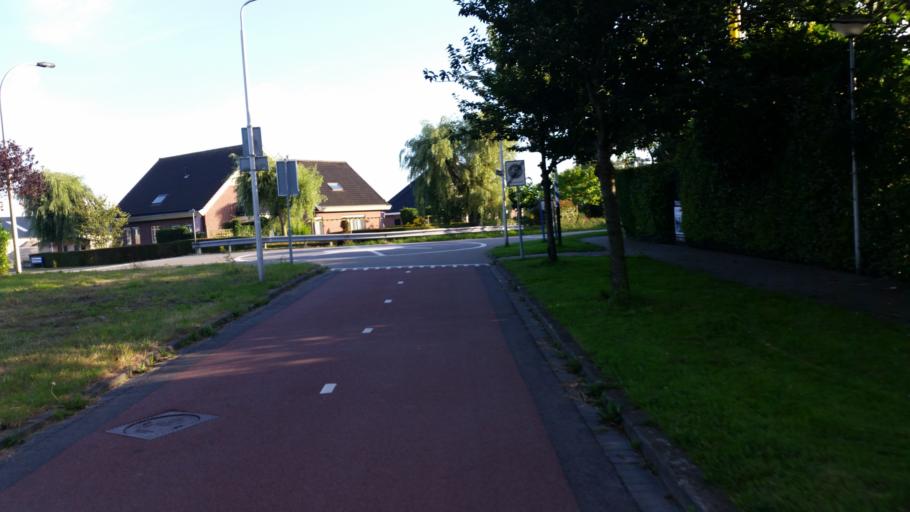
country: NL
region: South Holland
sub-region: Gemeente Den Haag
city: Ypenburg
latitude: 52.0471
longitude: 4.4033
